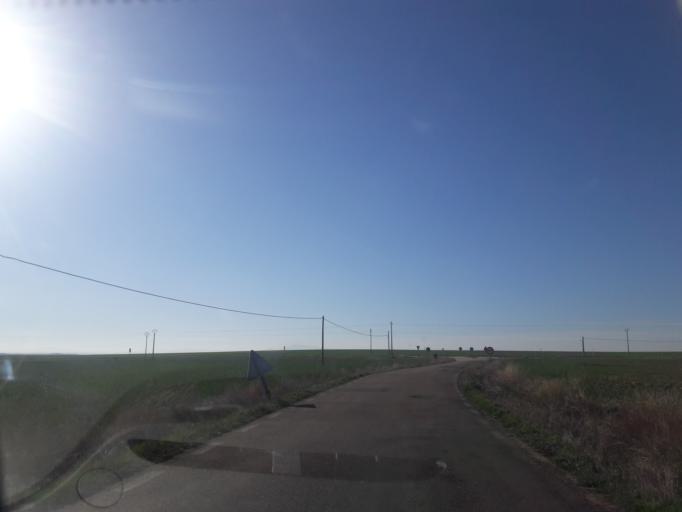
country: ES
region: Castille and Leon
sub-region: Provincia de Salamanca
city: Penarandilla
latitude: 40.8710
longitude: -5.3883
